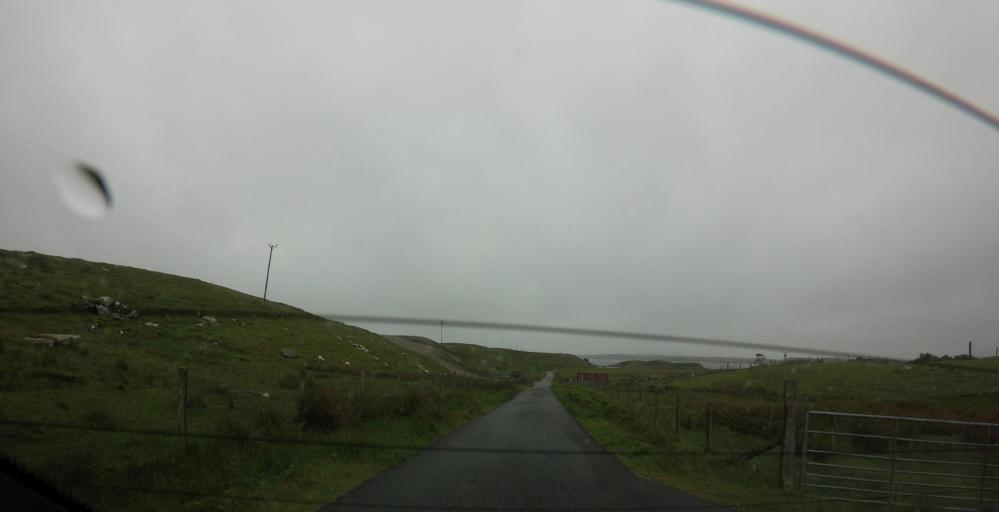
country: GB
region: Scotland
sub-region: Eilean Siar
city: Isle of North Uist
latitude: 57.5514
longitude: -7.2055
